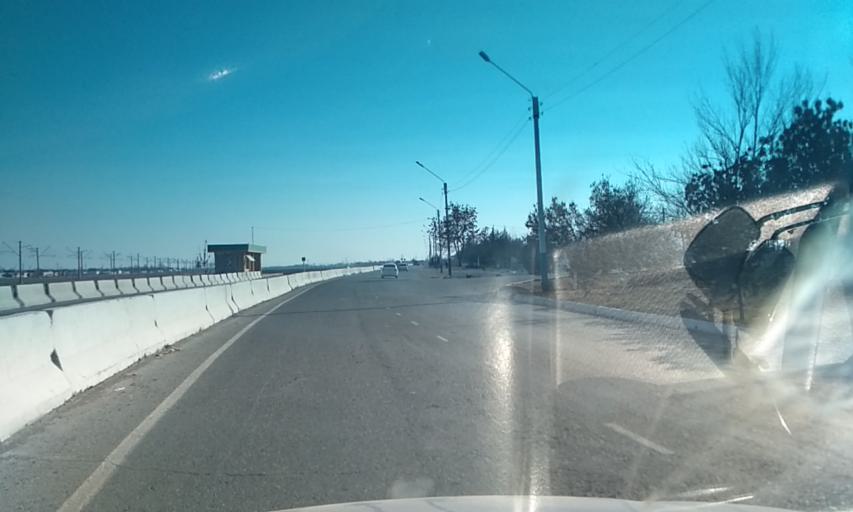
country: UZ
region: Sirdaryo
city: Guliston
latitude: 40.4705
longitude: 68.7719
